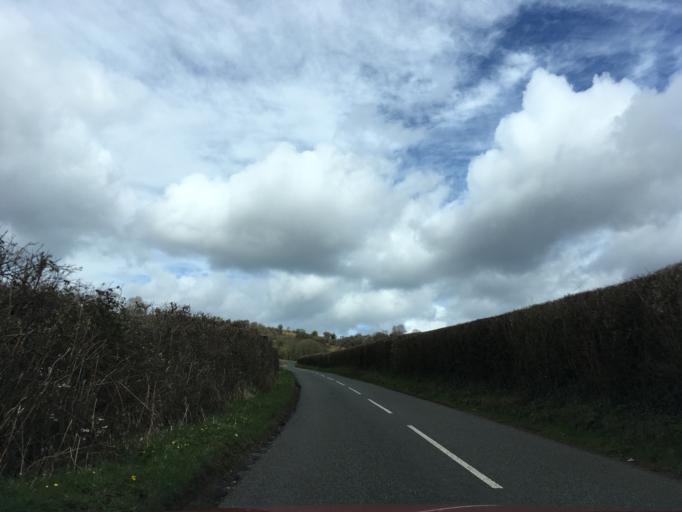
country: GB
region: England
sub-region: Gloucestershire
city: Coleford
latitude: 51.7491
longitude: -2.6456
